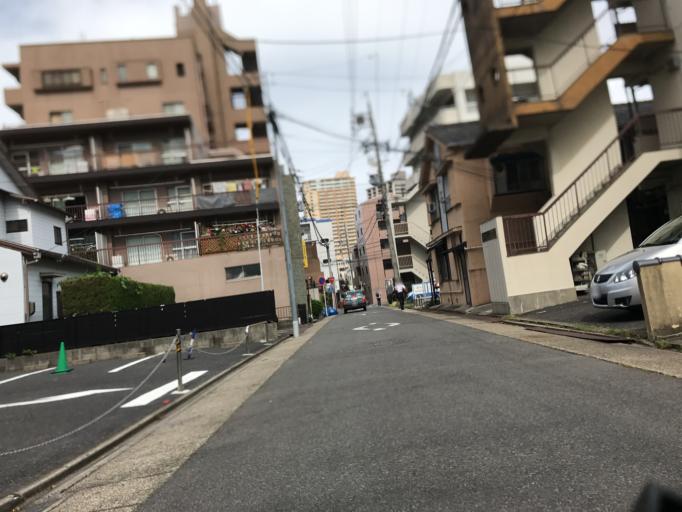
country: JP
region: Aichi
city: Nagoya-shi
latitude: 35.1681
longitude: 136.9336
